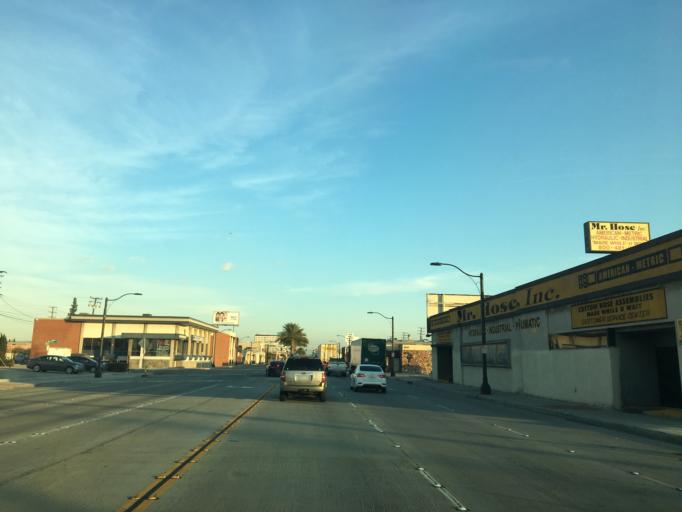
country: US
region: California
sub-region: Los Angeles County
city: Commerce
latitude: 34.0002
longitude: -118.1592
